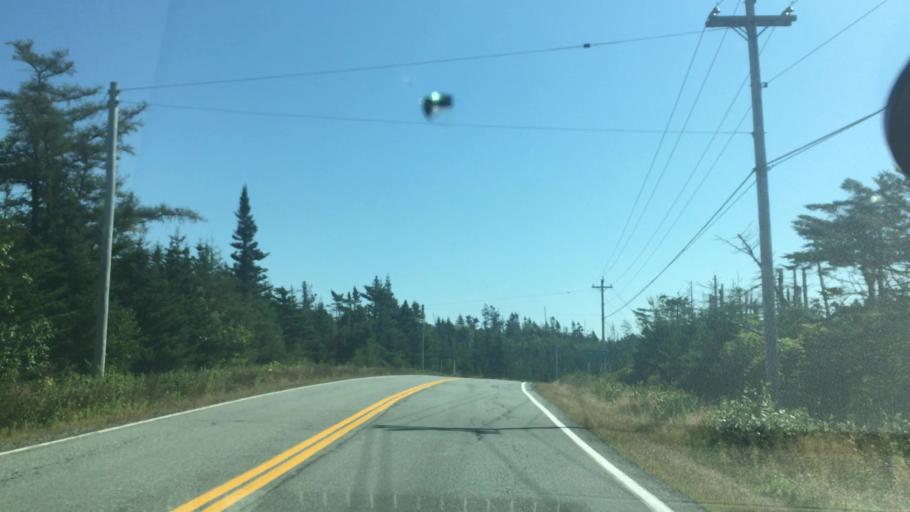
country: CA
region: Nova Scotia
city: New Glasgow
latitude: 44.9173
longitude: -62.3218
